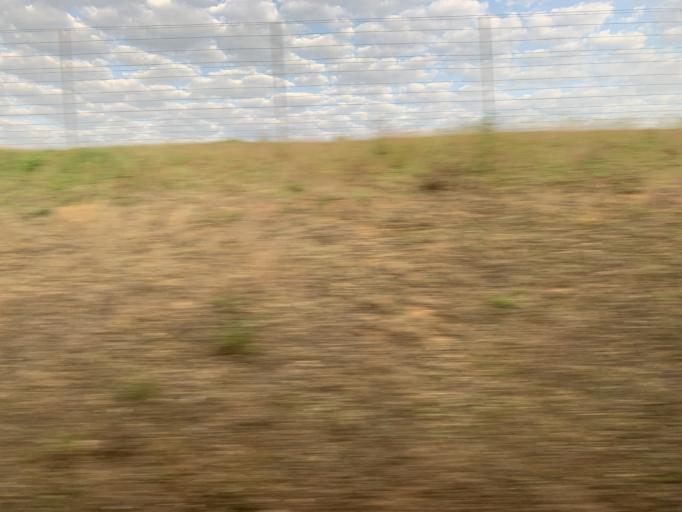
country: FR
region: Rhone-Alpes
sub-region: Departement du Rhone
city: Pusignan
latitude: 45.7321
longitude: 5.0771
